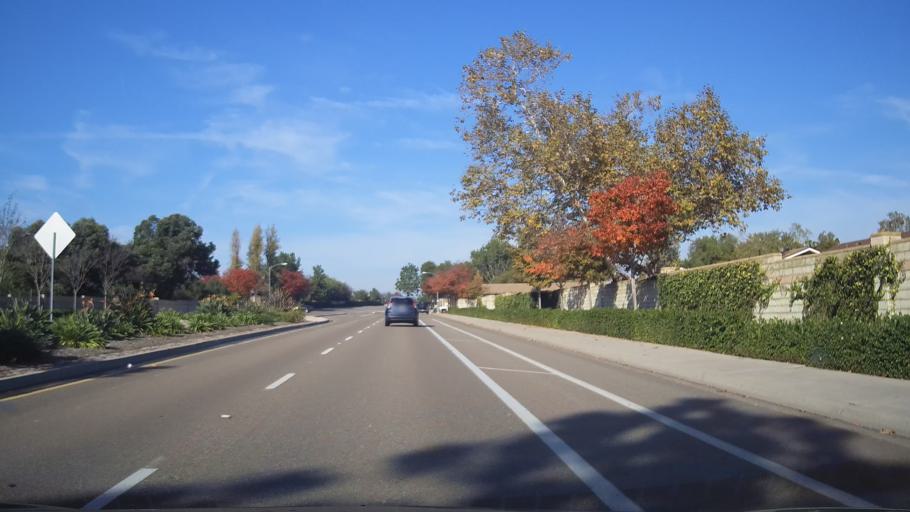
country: US
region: California
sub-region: San Diego County
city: La Mesa
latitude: 32.8114
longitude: -117.1056
